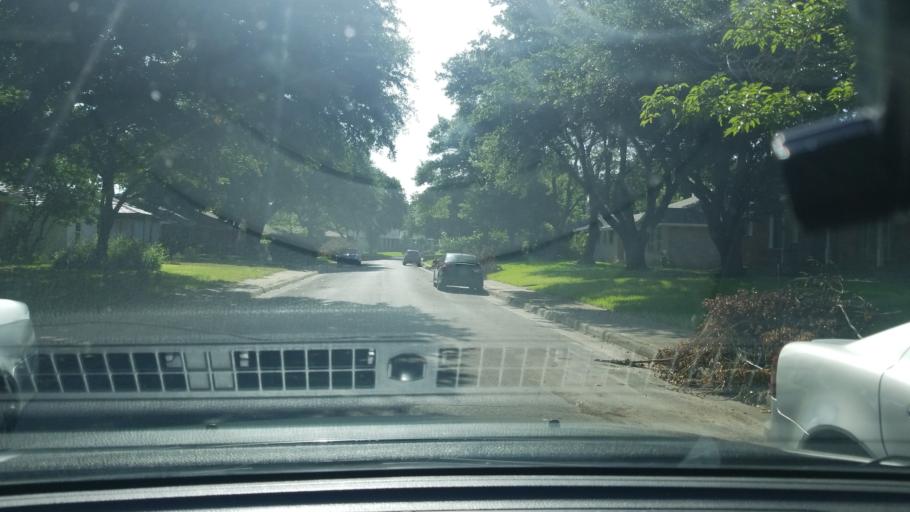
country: US
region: Texas
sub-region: Dallas County
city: Mesquite
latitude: 32.8093
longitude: -96.6759
